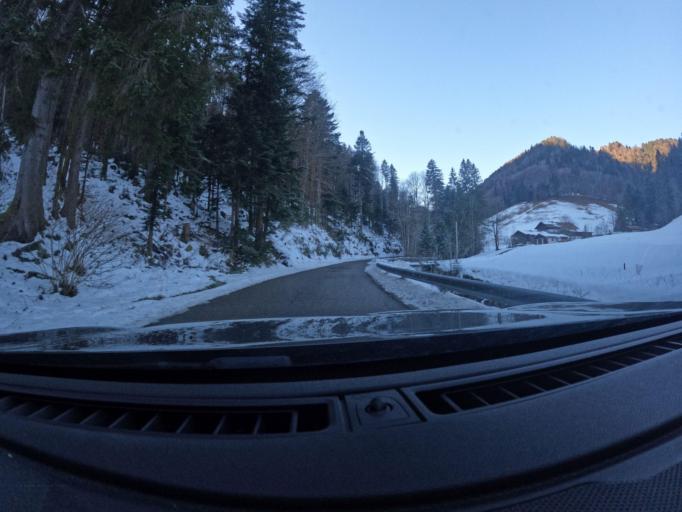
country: DE
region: Bavaria
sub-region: Upper Bavaria
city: Ruhpolding
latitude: 47.7624
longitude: 12.6096
